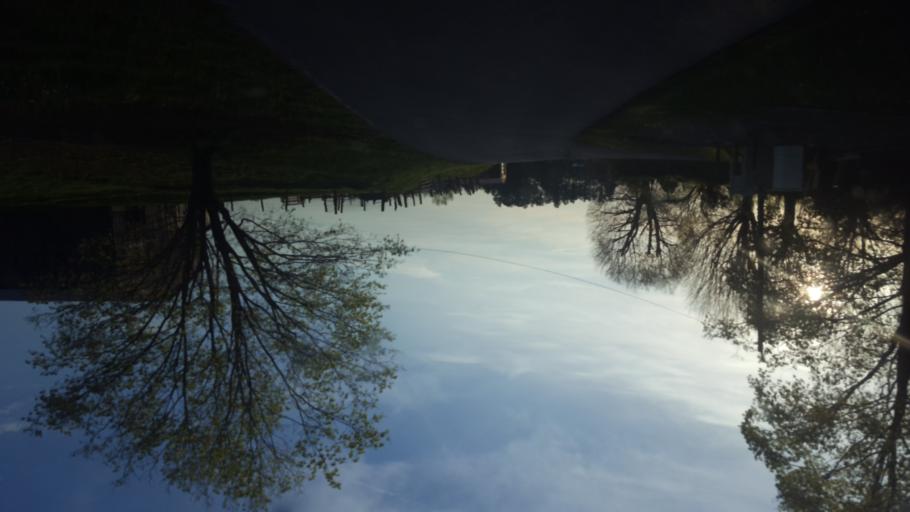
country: US
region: Kentucky
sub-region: Barren County
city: Cave City
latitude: 37.2143
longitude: -86.0022
